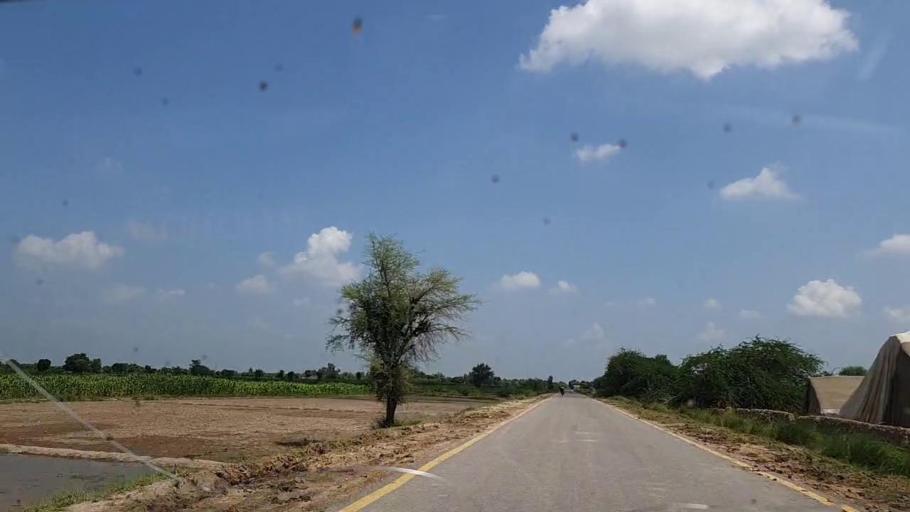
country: PK
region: Sindh
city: Tharu Shah
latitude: 26.9717
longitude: 68.0904
